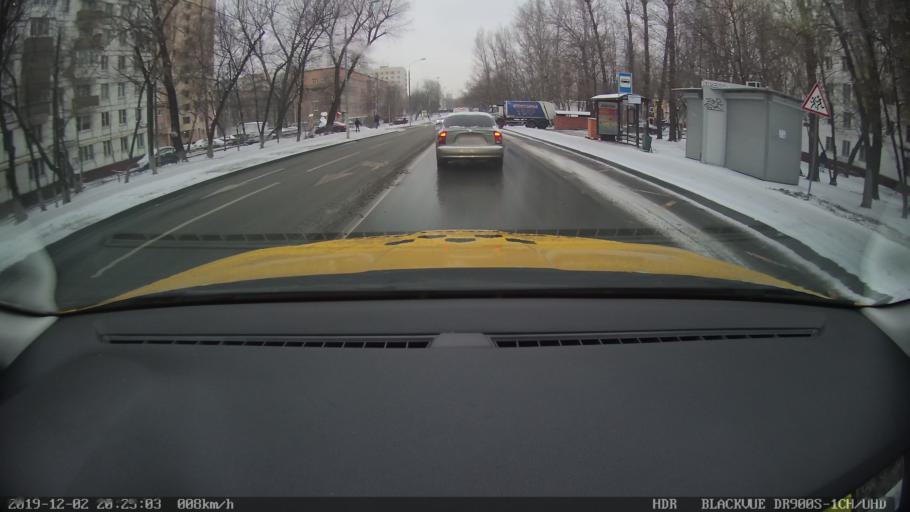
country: RU
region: Moscow
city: Novyye Kuz'minki
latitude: 55.7109
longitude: 37.7625
